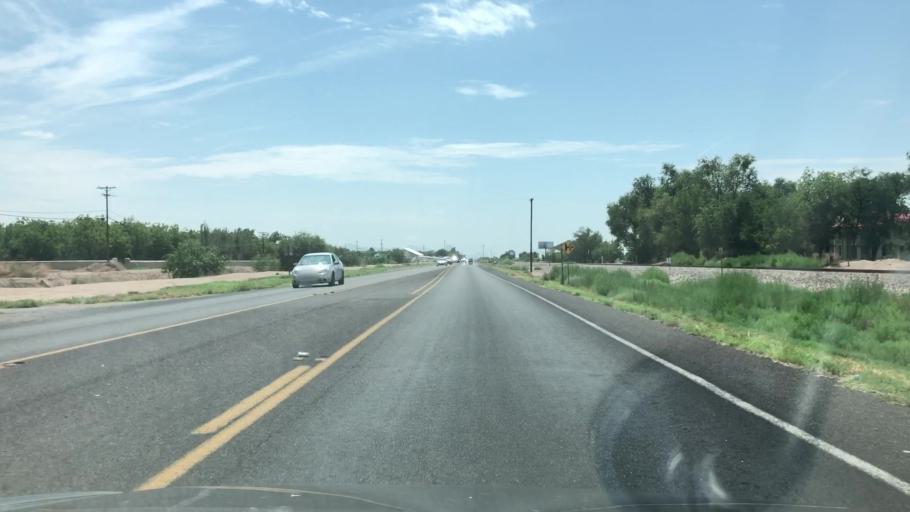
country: US
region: New Mexico
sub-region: Dona Ana County
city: University Park
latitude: 32.2588
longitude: -106.7562
